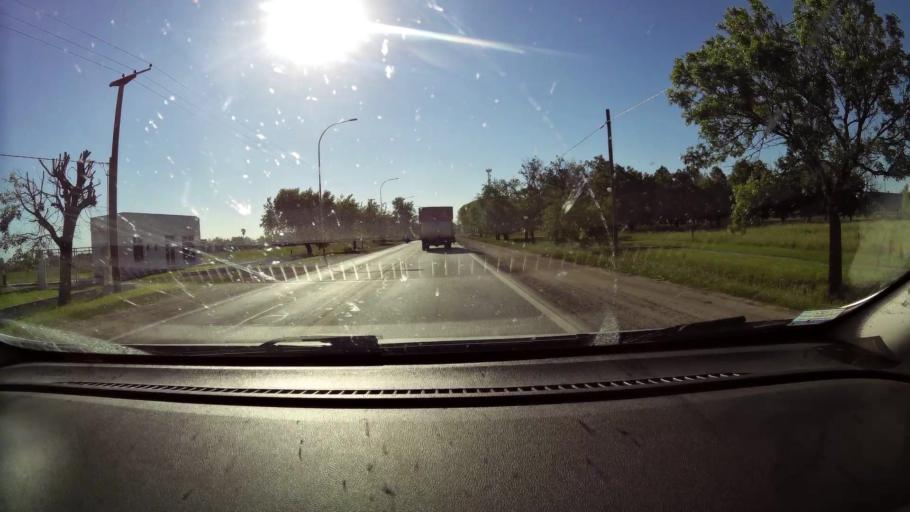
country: AR
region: Cordoba
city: San Francisco
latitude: -31.4187
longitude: -62.0713
